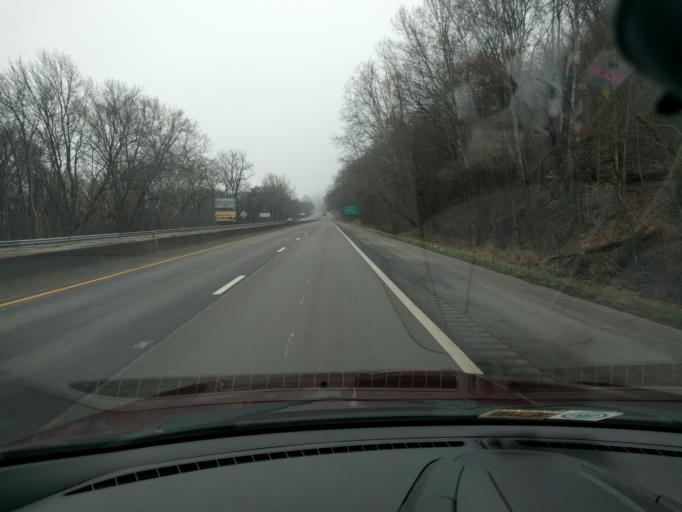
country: US
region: West Virginia
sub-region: Kanawha County
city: Rand
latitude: 38.2907
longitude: -81.5595
